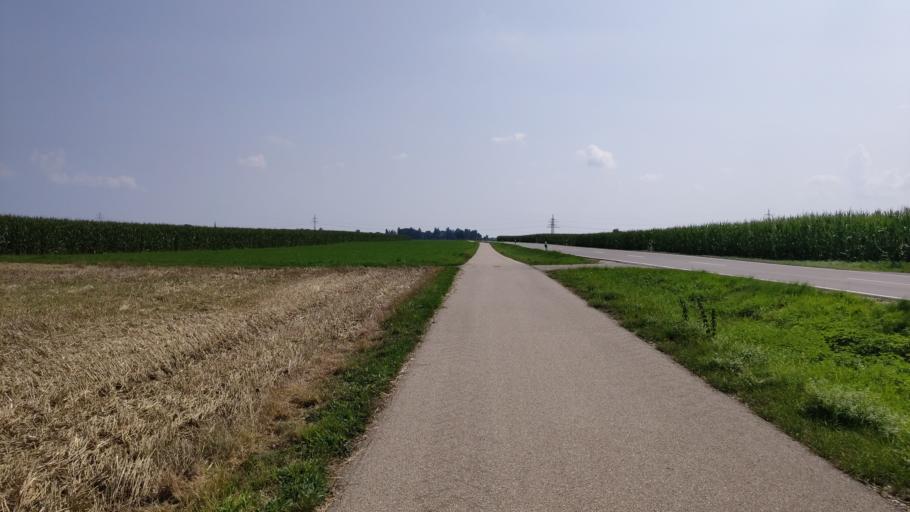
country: DE
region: Bavaria
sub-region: Swabia
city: Kleinaitingen
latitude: 48.2183
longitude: 10.8183
